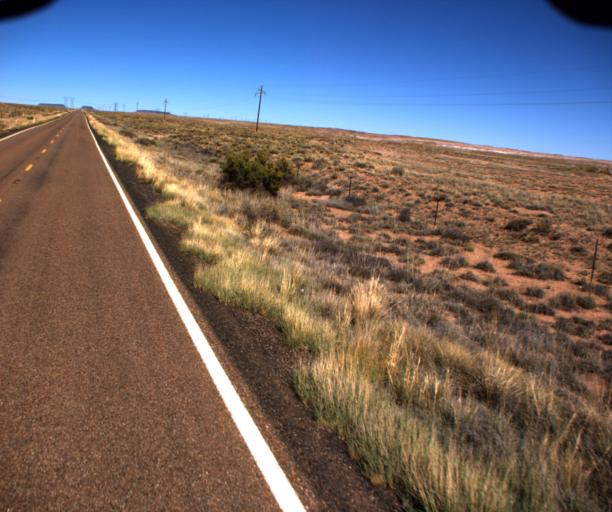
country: US
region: Arizona
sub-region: Navajo County
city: Holbrook
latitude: 35.1460
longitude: -110.0879
